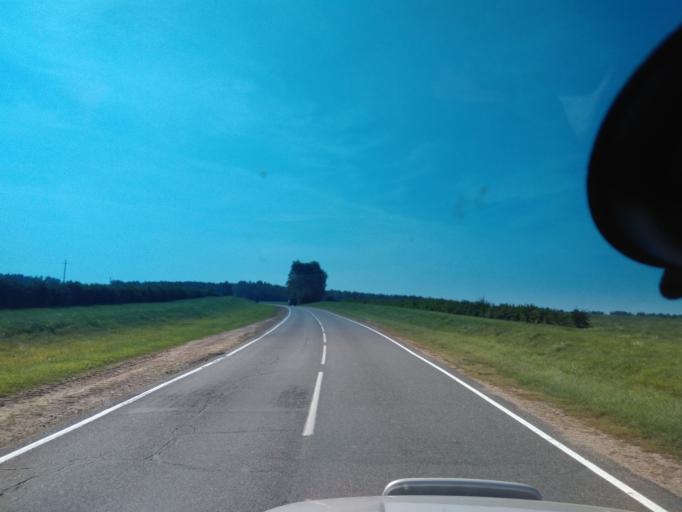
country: BY
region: Minsk
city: Uzda
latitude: 53.3625
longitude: 27.2260
